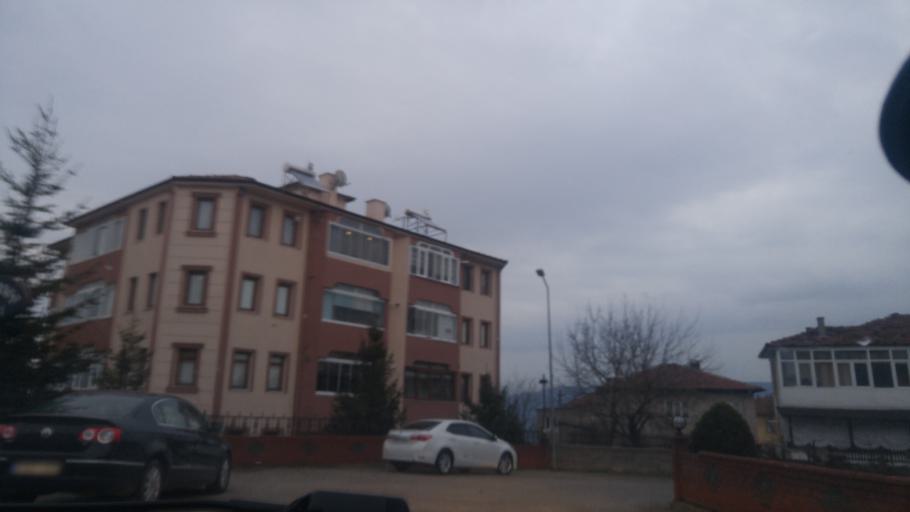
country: TR
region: Karabuk
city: Safranbolu
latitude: 41.2593
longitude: 32.6827
